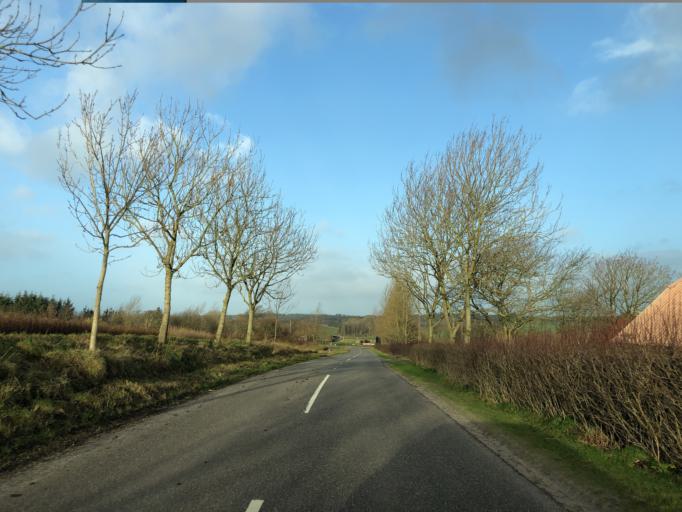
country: DK
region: Central Jutland
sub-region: Ringkobing-Skjern Kommune
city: Videbaek
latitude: 56.1925
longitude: 8.5421
